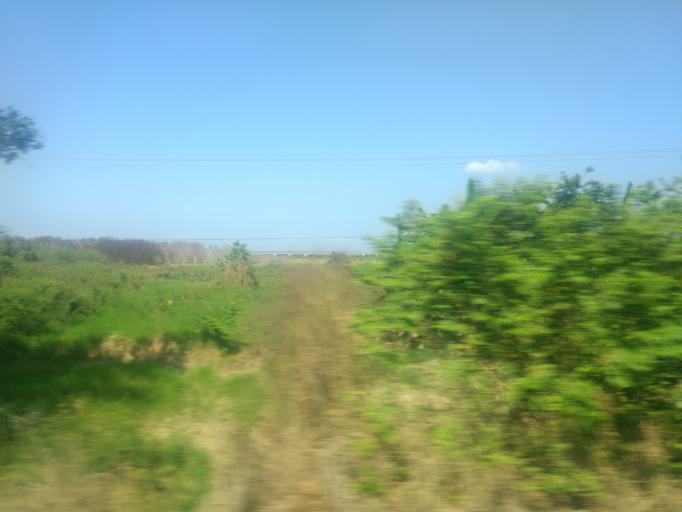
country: MX
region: Colima
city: El Colomo
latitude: 19.0459
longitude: -104.2617
